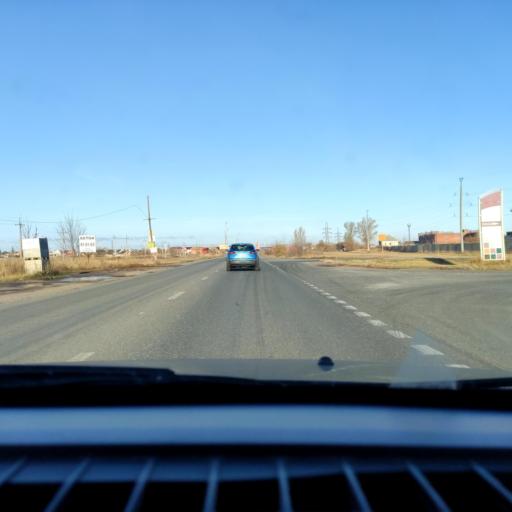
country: RU
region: Samara
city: Tol'yatti
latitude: 53.5693
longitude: 49.3453
